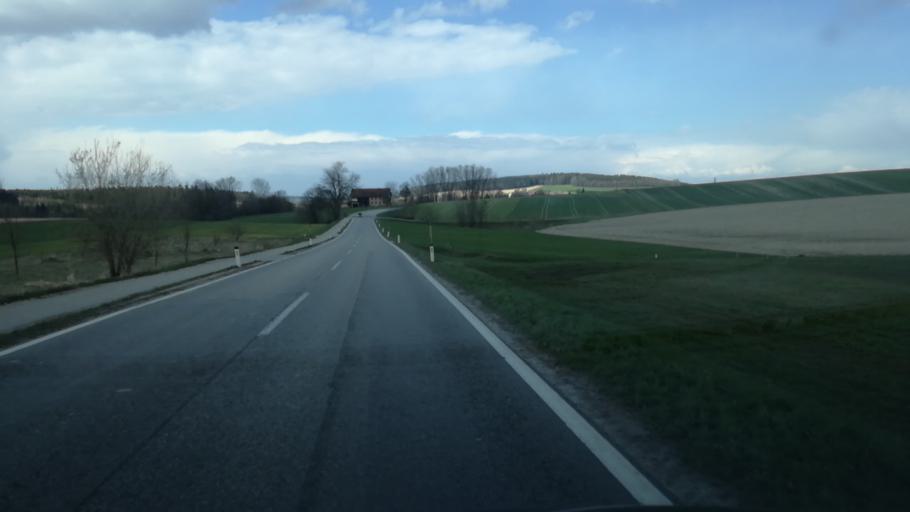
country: AT
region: Upper Austria
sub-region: Politischer Bezirk Ried im Innkreis
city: Ried im Innkreis
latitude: 48.1588
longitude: 13.4841
